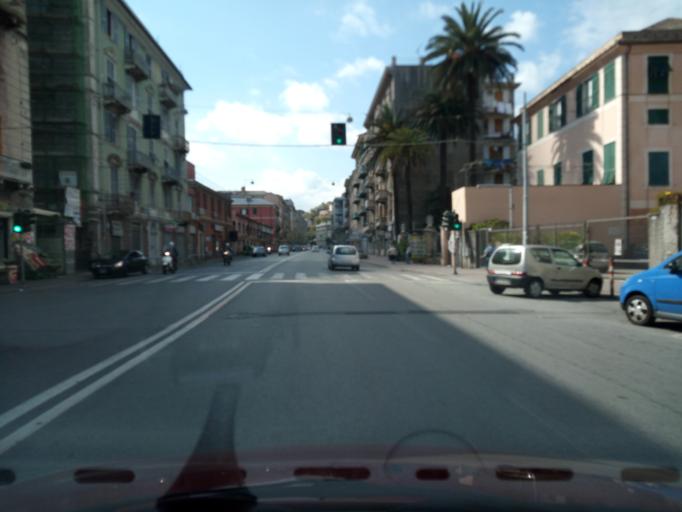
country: IT
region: Liguria
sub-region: Provincia di Genova
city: San Teodoro
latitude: 44.4259
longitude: 8.8439
